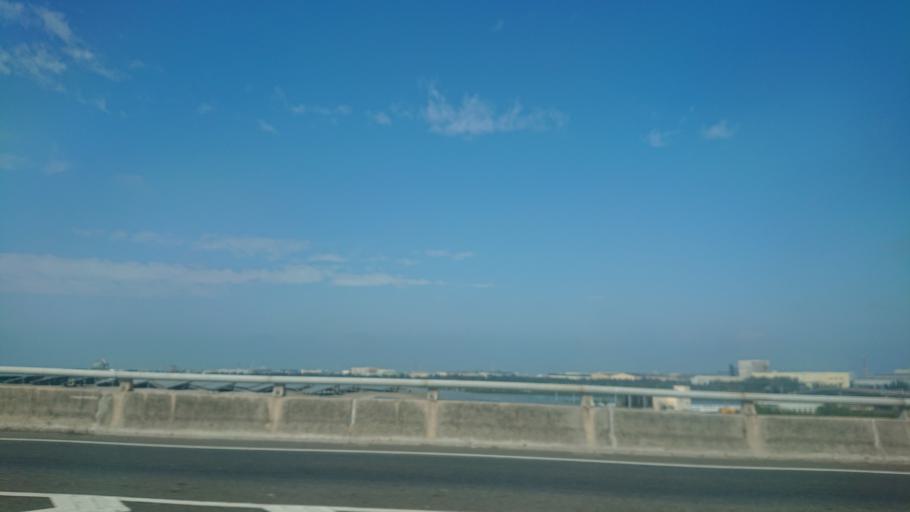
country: TW
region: Taiwan
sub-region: Changhua
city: Chang-hua
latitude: 24.0596
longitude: 120.4095
